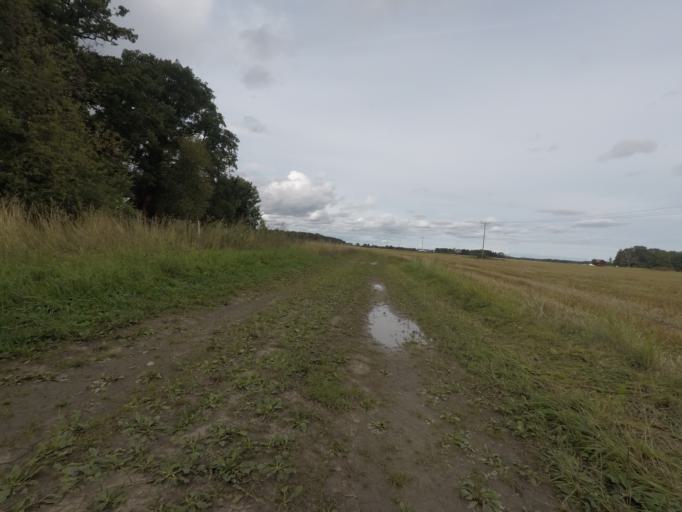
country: SE
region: Vaestmanland
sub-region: Kungsors Kommun
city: Kungsoer
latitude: 59.4559
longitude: 16.0500
